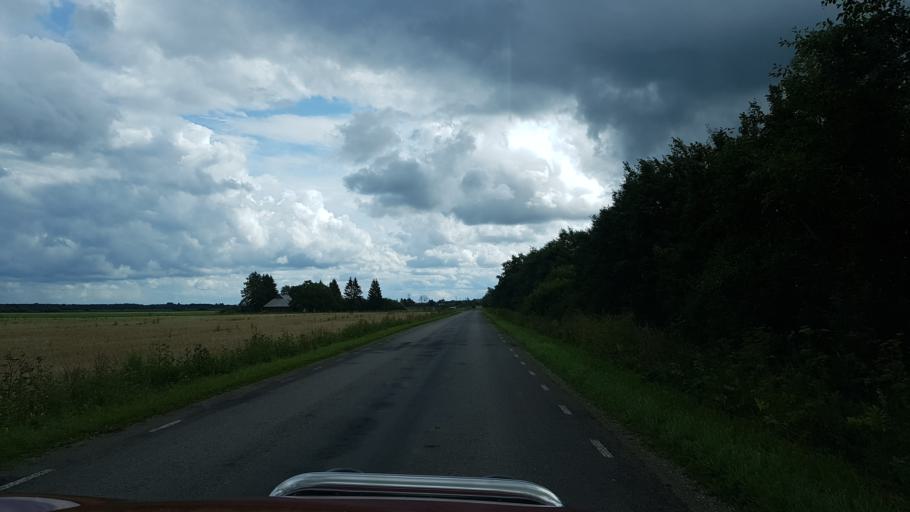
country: EE
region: Laeaene
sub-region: Lihula vald
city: Lihula
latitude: 58.7195
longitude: 23.9795
